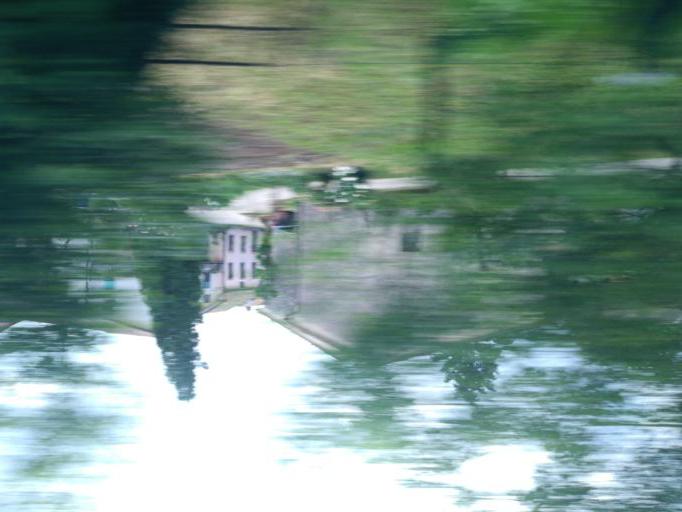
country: IT
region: Veneto
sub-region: Provincia di Vicenza
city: Giavenale
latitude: 45.7097
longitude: 11.3979
